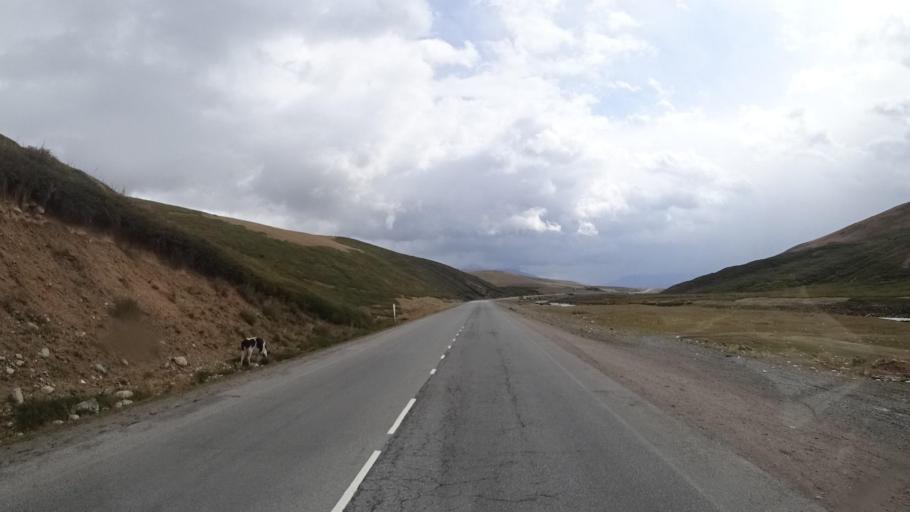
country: KG
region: Jalal-Abad
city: Uch-Terek
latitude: 42.2079
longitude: 73.2539
